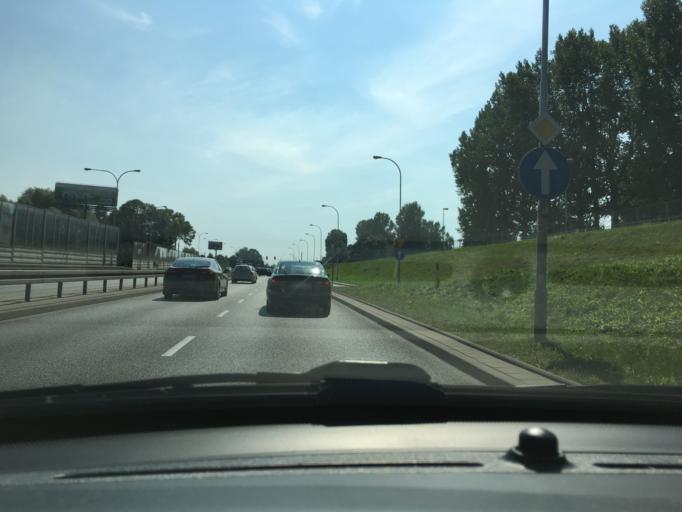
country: PL
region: Masovian Voivodeship
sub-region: Warszawa
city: Praga Poludnie
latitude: 52.2137
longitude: 21.1026
